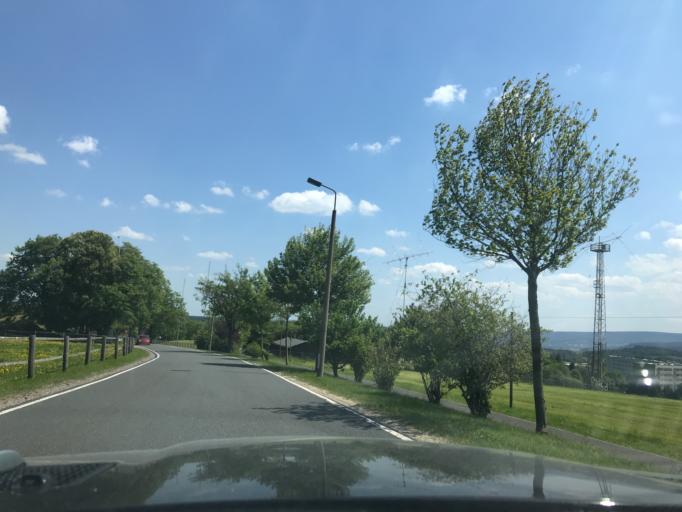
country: DE
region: Thuringia
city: Ilmenau
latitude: 50.7012
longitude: 10.9193
